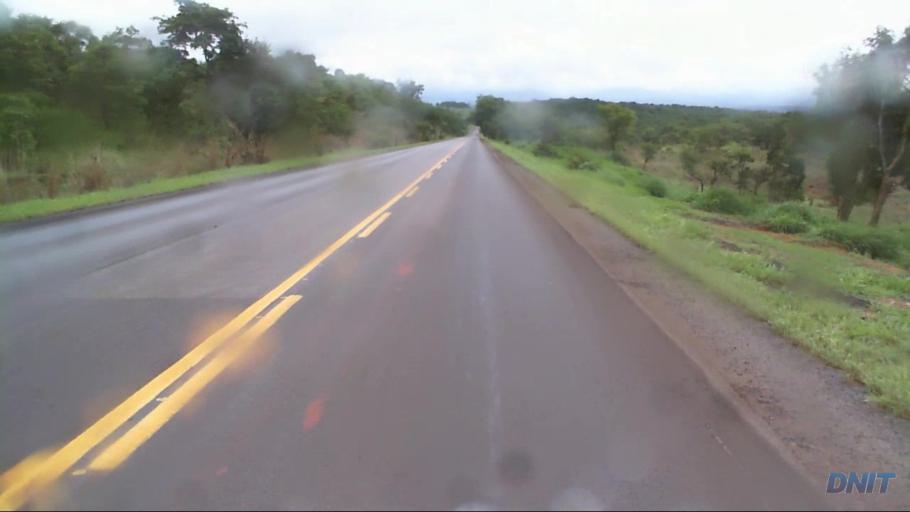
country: BR
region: Goias
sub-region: Padre Bernardo
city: Padre Bernardo
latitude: -15.1928
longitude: -48.4381
